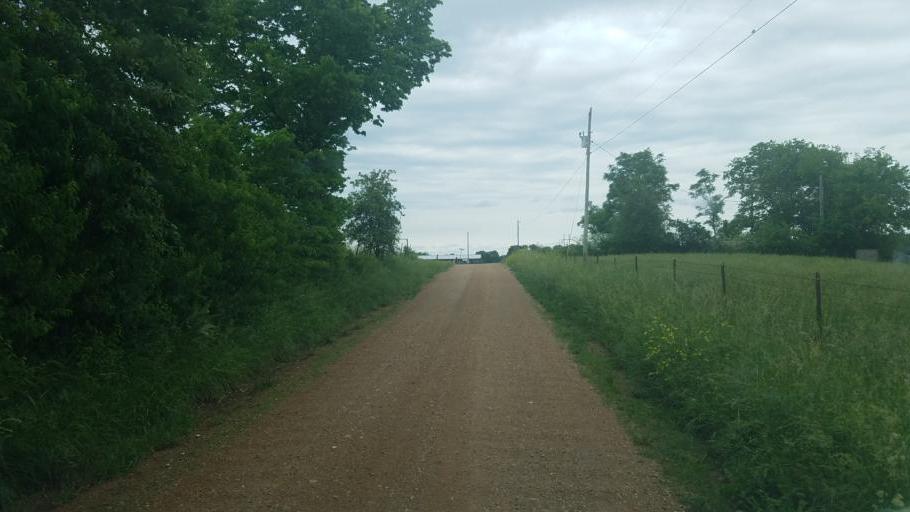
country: US
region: Missouri
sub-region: Moniteau County
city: California
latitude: 38.5961
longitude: -92.6477
